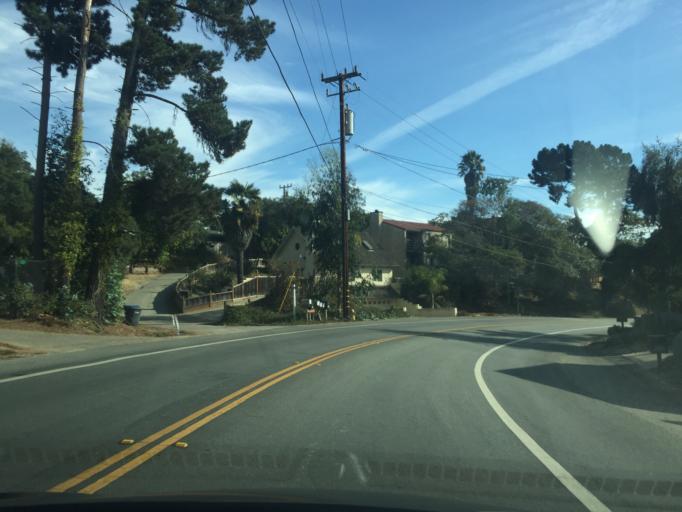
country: US
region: California
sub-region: Santa Cruz County
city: La Selva Beach
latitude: 36.9397
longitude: -121.8579
